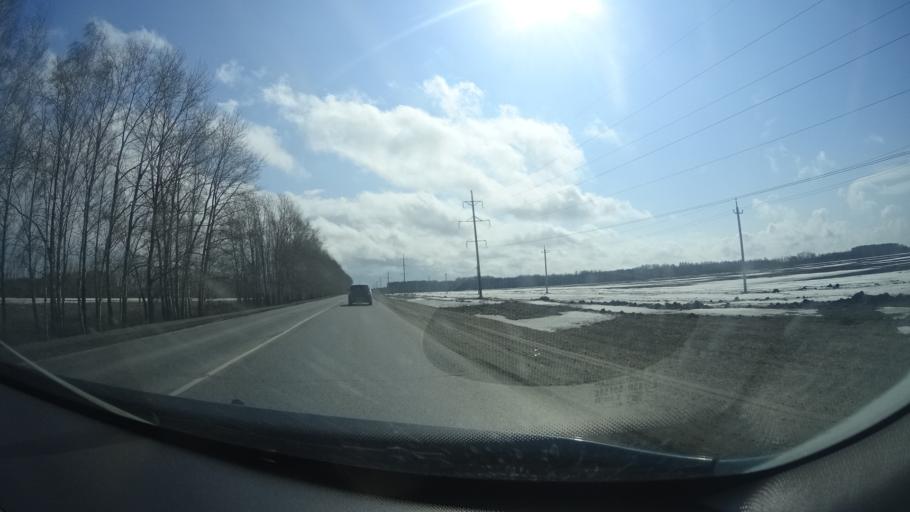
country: RU
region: Bashkortostan
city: Mikhaylovka
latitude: 54.8530
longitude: 55.7702
